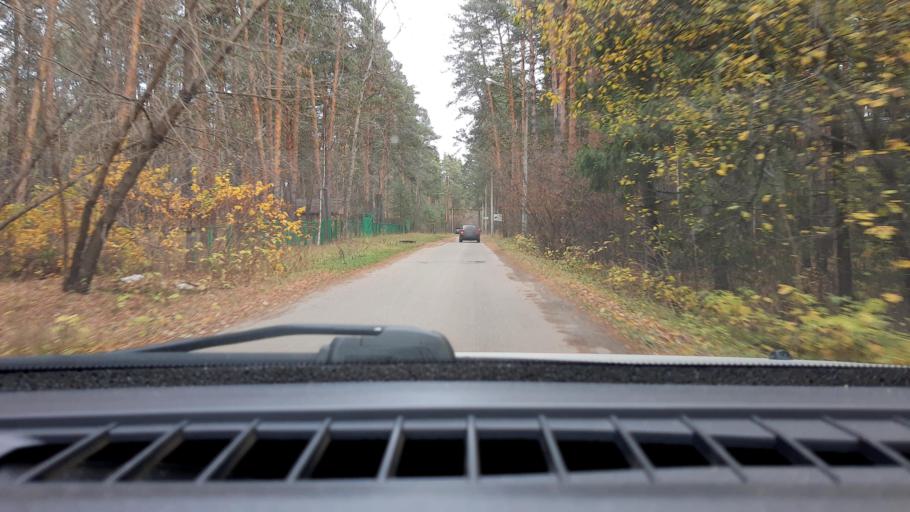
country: RU
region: Nizjnij Novgorod
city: Kstovo
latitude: 56.1677
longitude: 44.1174
